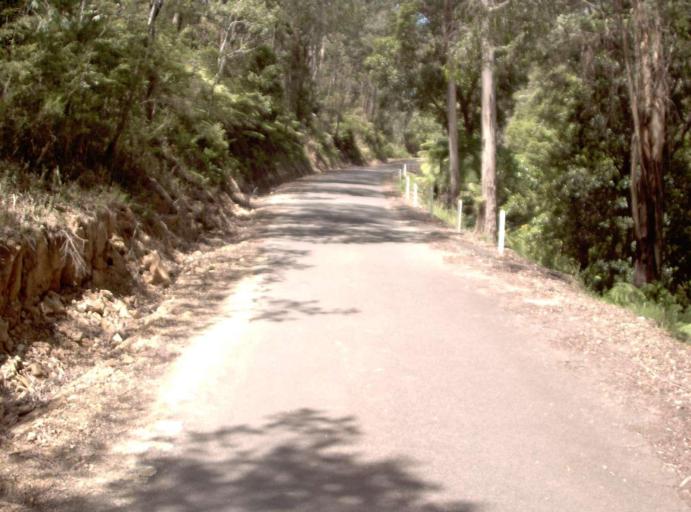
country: AU
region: New South Wales
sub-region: Bombala
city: Bombala
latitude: -37.4424
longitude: 148.9615
